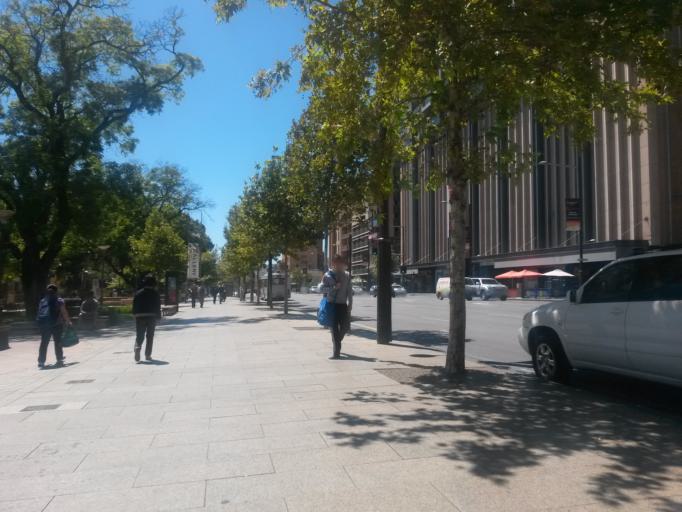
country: AU
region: South Australia
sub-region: Adelaide
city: Adelaide
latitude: -34.9213
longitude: 138.6029
